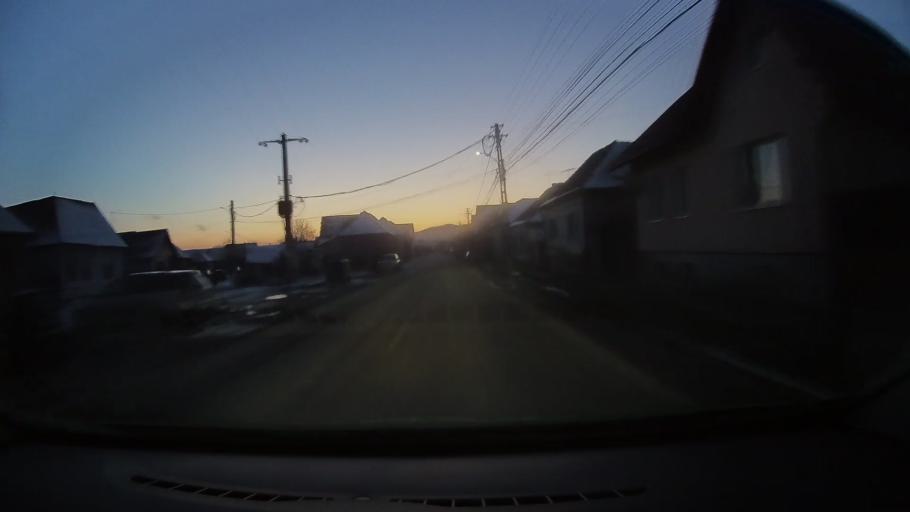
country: RO
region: Sibiu
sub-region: Comuna Darlos
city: Darlos
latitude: 46.1860
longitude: 24.4045
